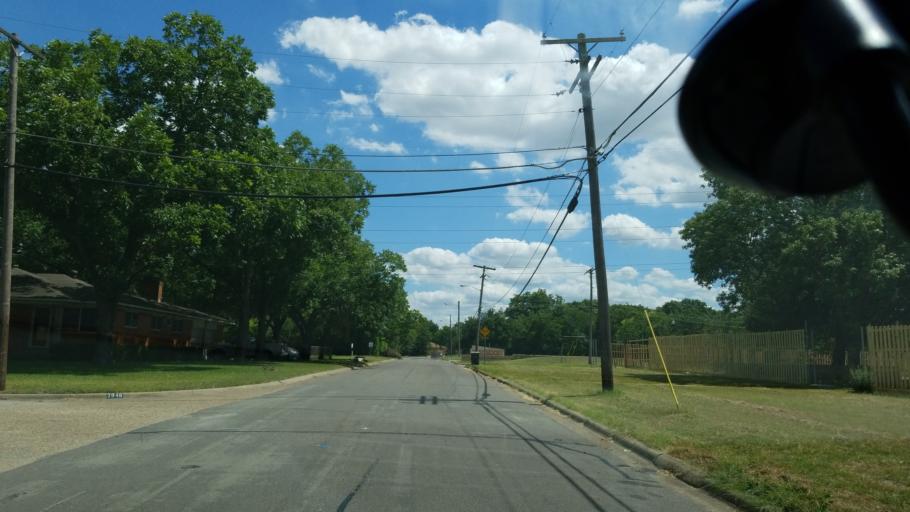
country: US
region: Texas
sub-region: Dallas County
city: Cockrell Hill
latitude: 32.7002
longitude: -96.8702
